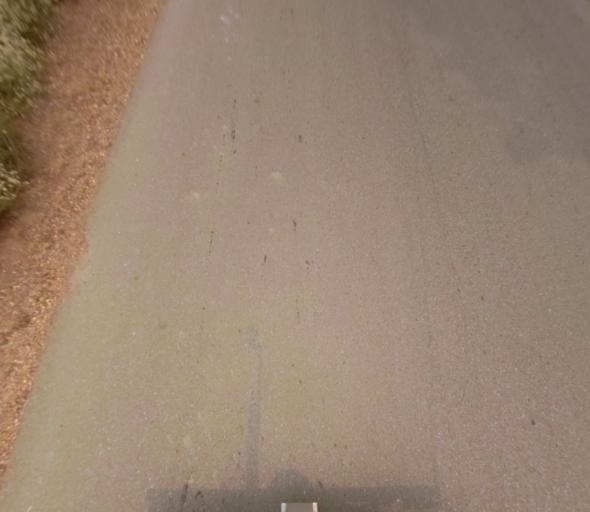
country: US
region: California
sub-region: Madera County
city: Oakhurst
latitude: 37.3313
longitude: -119.6299
